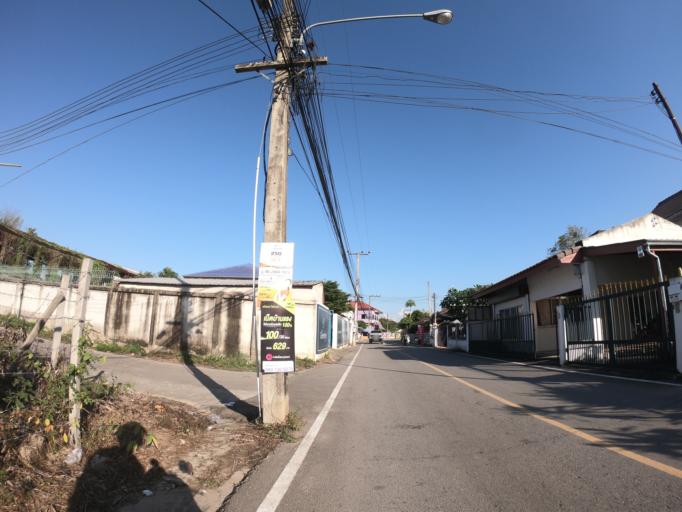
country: TH
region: Chiang Mai
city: San Sai
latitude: 18.8248
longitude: 99.0338
